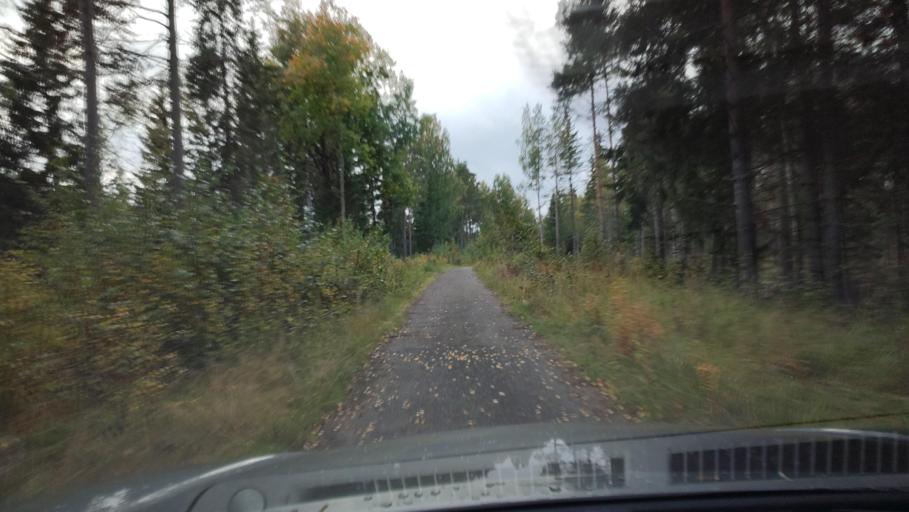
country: FI
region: Ostrobothnia
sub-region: Sydosterbotten
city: Kristinestad
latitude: 62.2674
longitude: 21.4183
